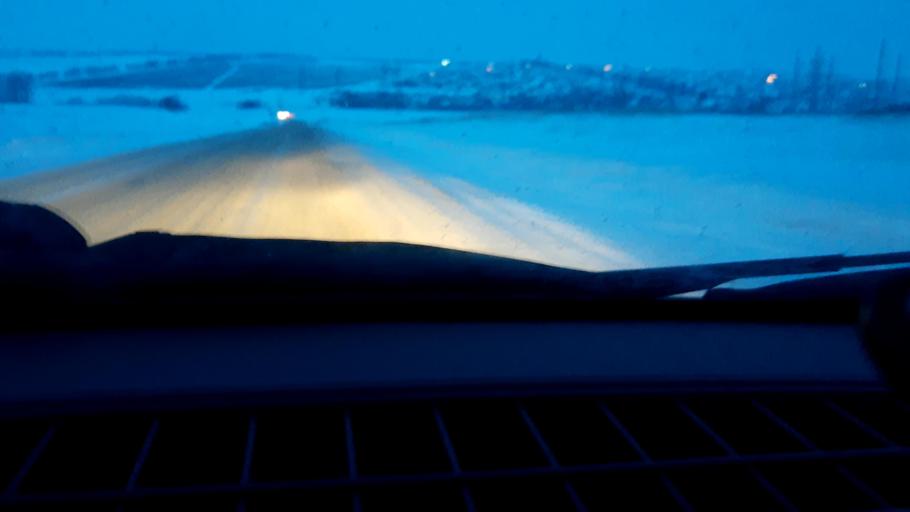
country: RU
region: Bashkortostan
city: Alekseyevka
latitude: 54.6786
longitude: 55.0154
